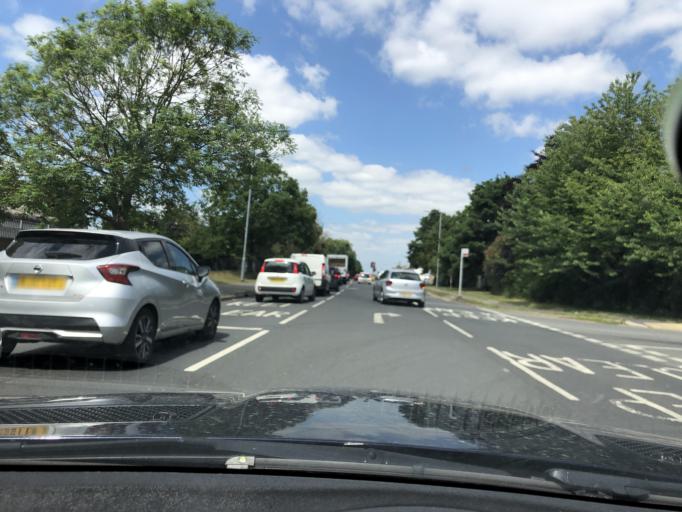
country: GB
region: England
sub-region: Essex
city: Chelmsford
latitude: 51.7254
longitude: 0.4517
